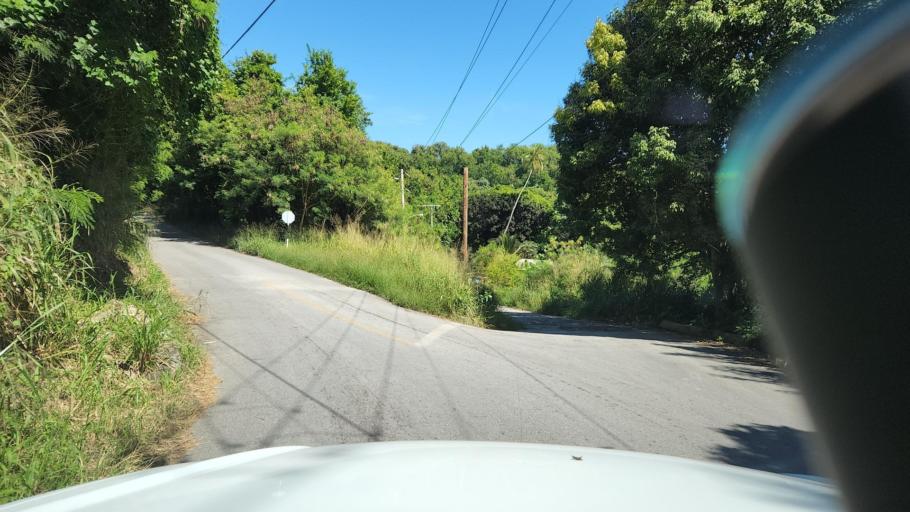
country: BB
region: Saint Joseph
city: Bathsheba
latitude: 13.2157
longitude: -59.5492
